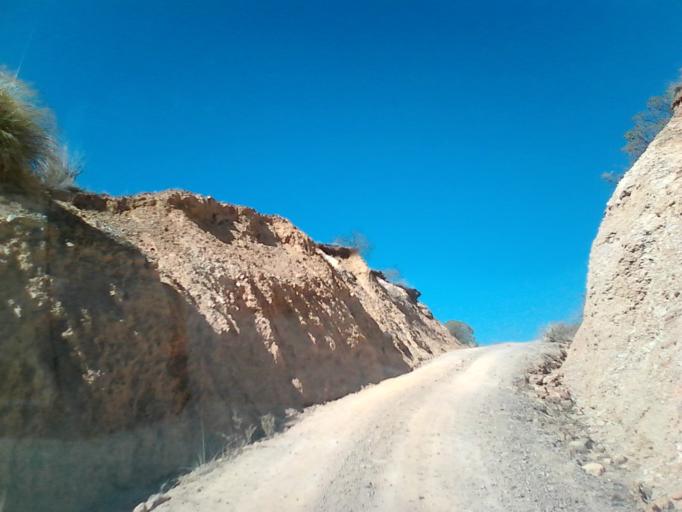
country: CO
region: Boyaca
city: Sachica
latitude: 5.5619
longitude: -73.5605
